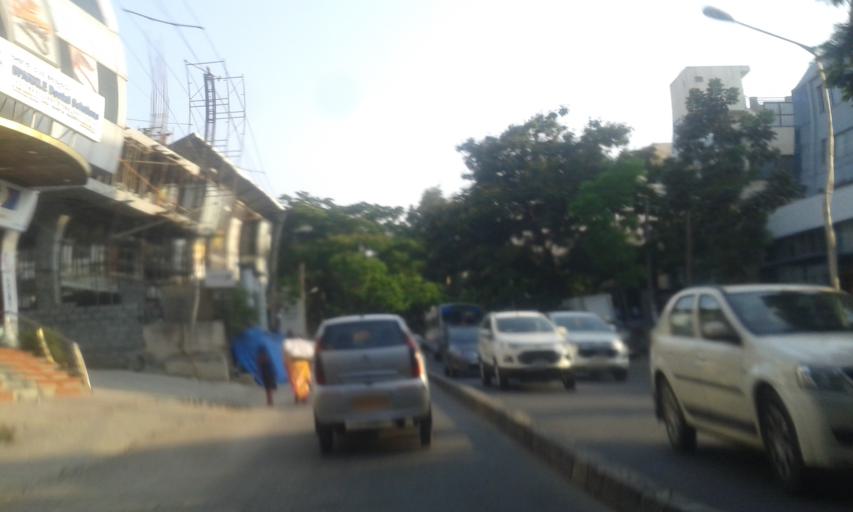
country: IN
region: Karnataka
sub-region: Bangalore Urban
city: Bangalore
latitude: 12.9536
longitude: 77.5800
